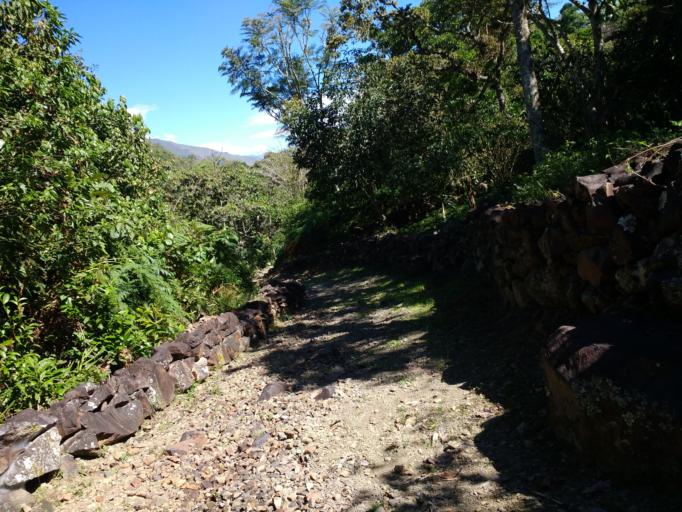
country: PE
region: Cusco
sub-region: Provincia de La Convencion
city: Maranura
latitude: -13.0046
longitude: -72.5325
